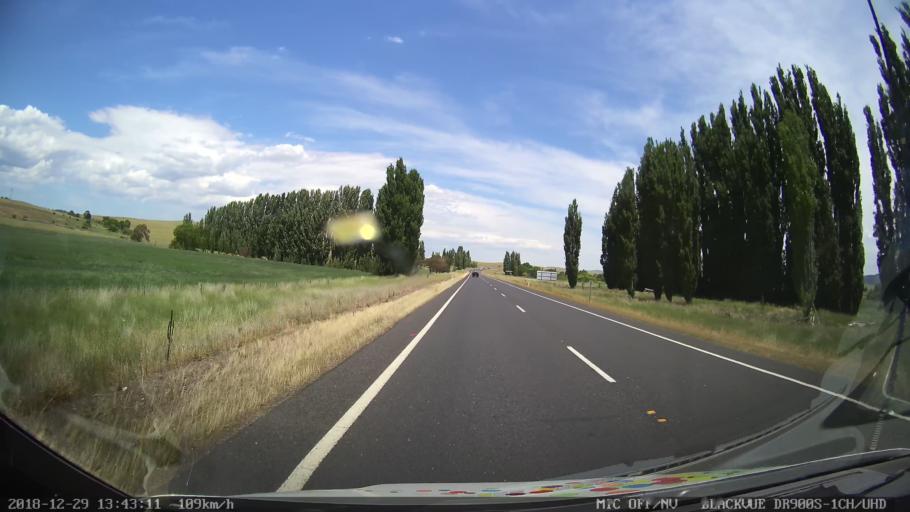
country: AU
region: New South Wales
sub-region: Cooma-Monaro
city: Cooma
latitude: -36.0687
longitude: 149.1587
